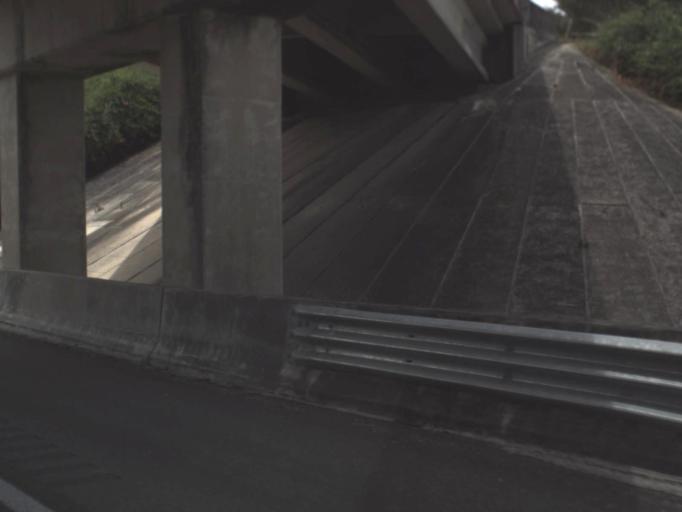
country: US
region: Florida
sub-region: Columbia County
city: Lake City
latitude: 30.0911
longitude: -82.6406
